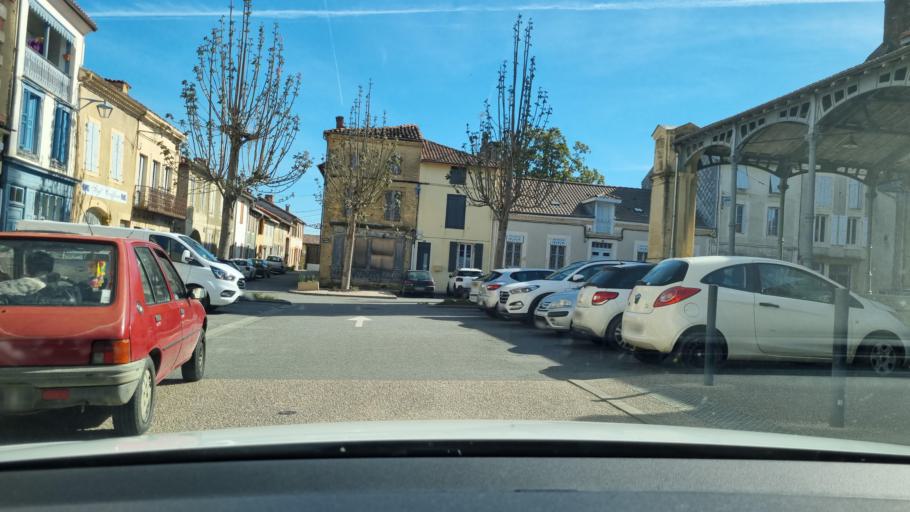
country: FR
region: Midi-Pyrenees
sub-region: Departement de la Haute-Garonne
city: Boulogne-sur-Gesse
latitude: 43.2907
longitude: 0.6452
